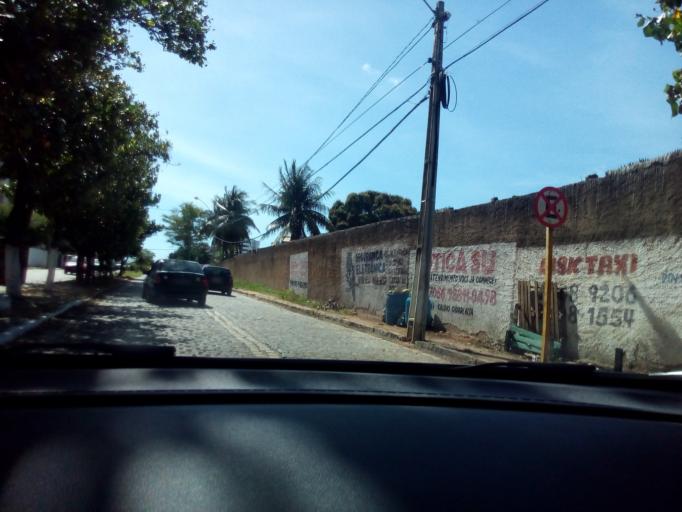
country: BR
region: Rio Grande do Norte
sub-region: Parnamirim
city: Parnamirim
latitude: -5.8859
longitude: -35.1997
